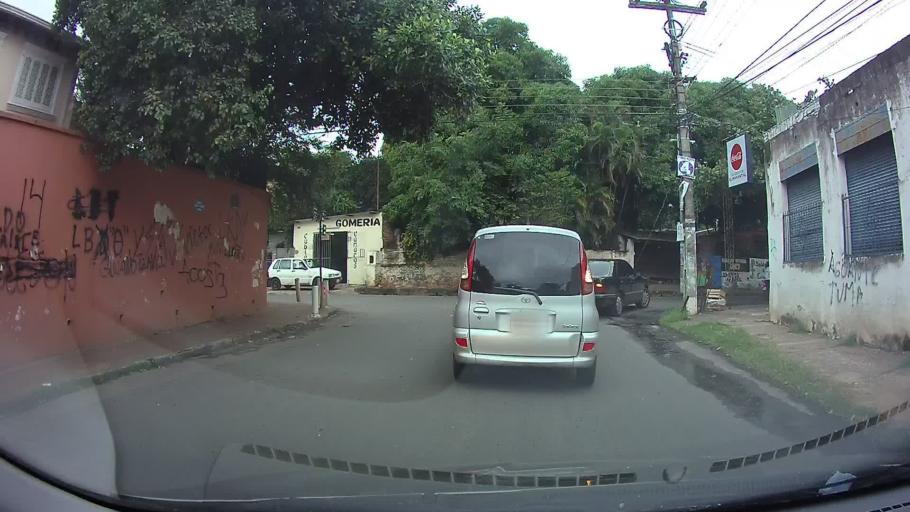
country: PY
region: Central
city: Lambare
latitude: -25.3216
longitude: -57.6096
